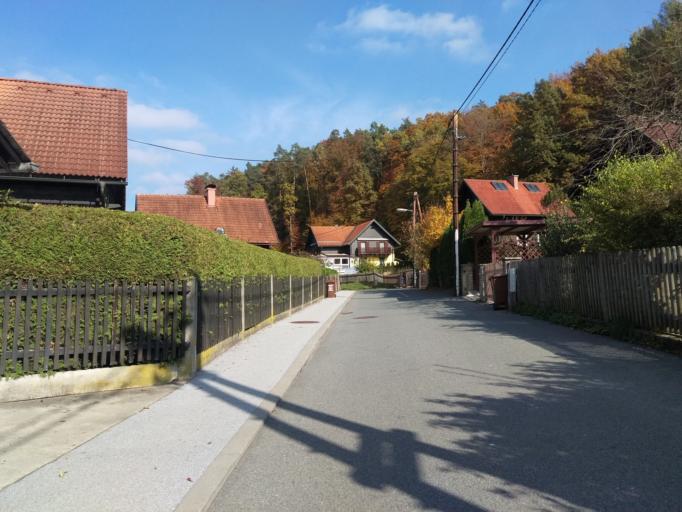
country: AT
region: Styria
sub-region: Graz Stadt
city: Mariatrost
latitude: 47.0952
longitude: 15.4688
